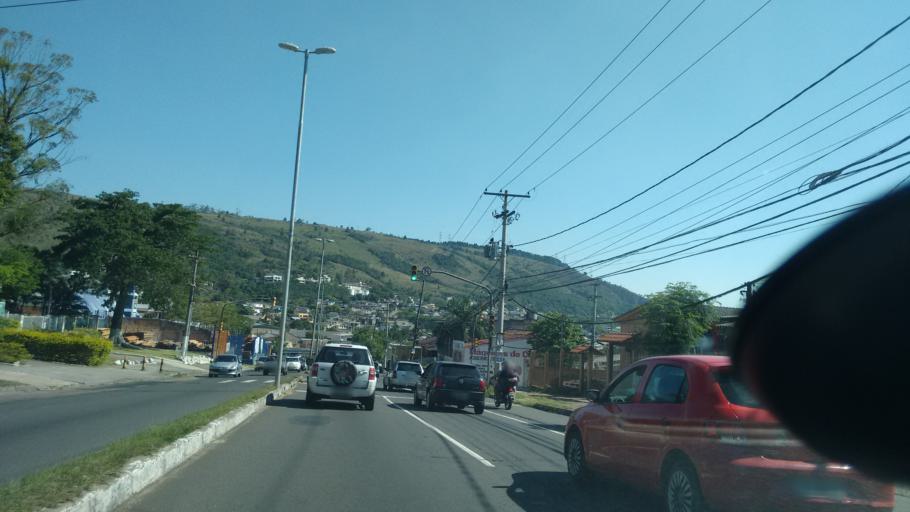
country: BR
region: Rio Grande do Sul
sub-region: Cachoeirinha
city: Cachoeirinha
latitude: -30.0366
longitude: -51.1220
